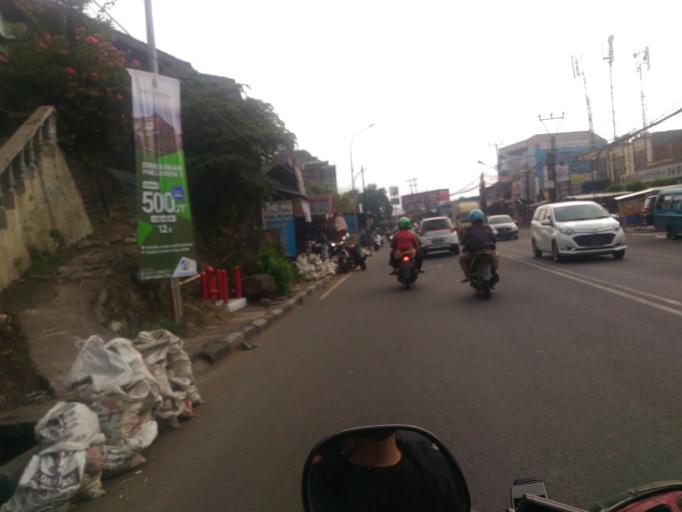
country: ID
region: West Java
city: Bogor
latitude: -6.5611
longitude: 106.8122
